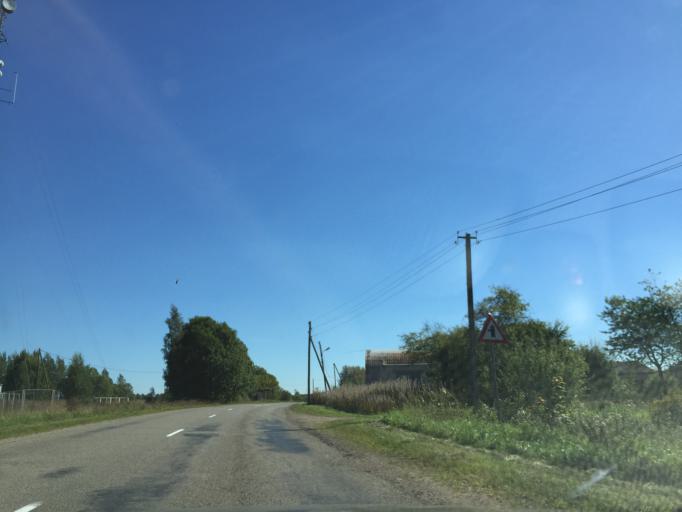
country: LV
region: Akniste
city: Akniste
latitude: 56.0531
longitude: 25.9050
